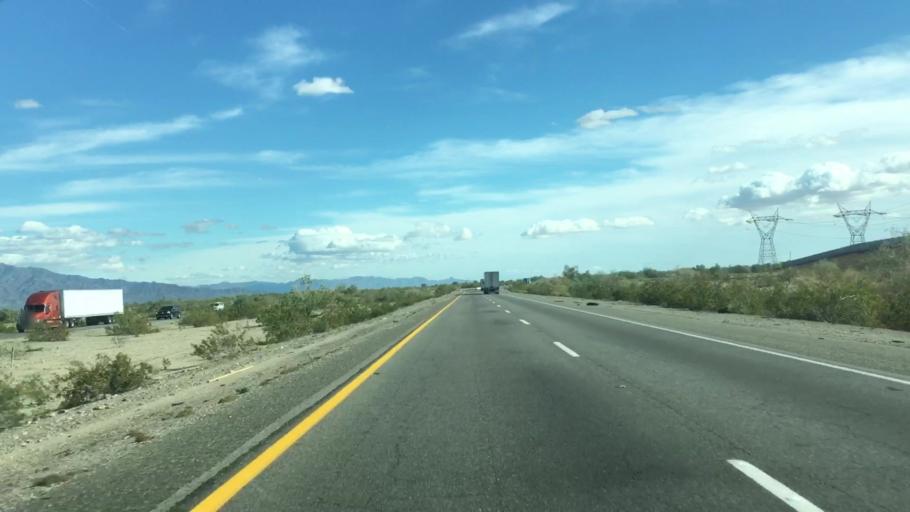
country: US
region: California
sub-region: Imperial County
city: Niland
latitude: 33.7019
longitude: -115.3124
